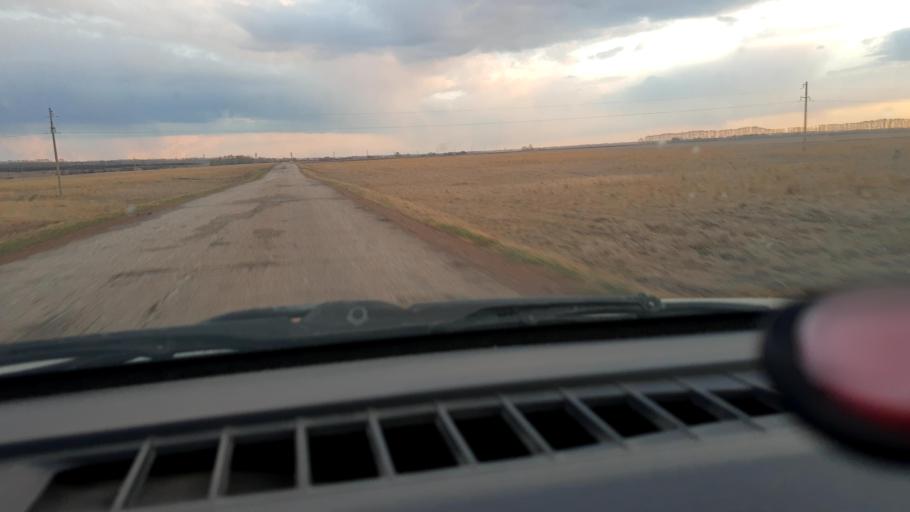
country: RU
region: Bashkortostan
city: Asanovo
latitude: 54.9560
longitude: 55.5340
